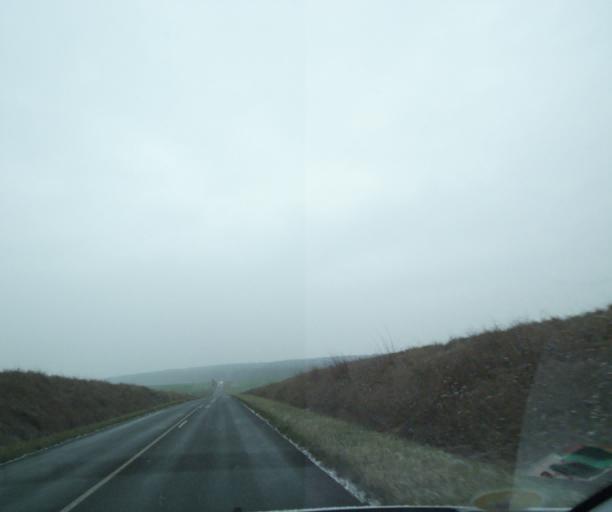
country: FR
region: Champagne-Ardenne
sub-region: Departement de la Haute-Marne
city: Wassy
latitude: 48.4802
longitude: 5.0026
